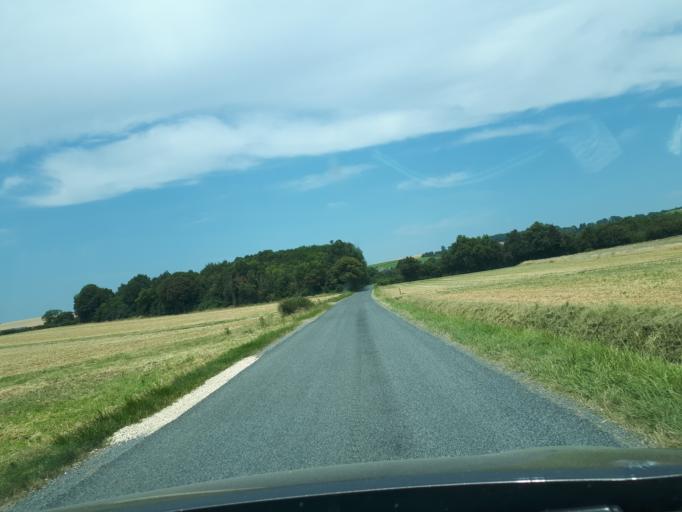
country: FR
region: Centre
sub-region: Departement du Cher
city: Sancerre
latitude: 47.2958
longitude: 2.7506
